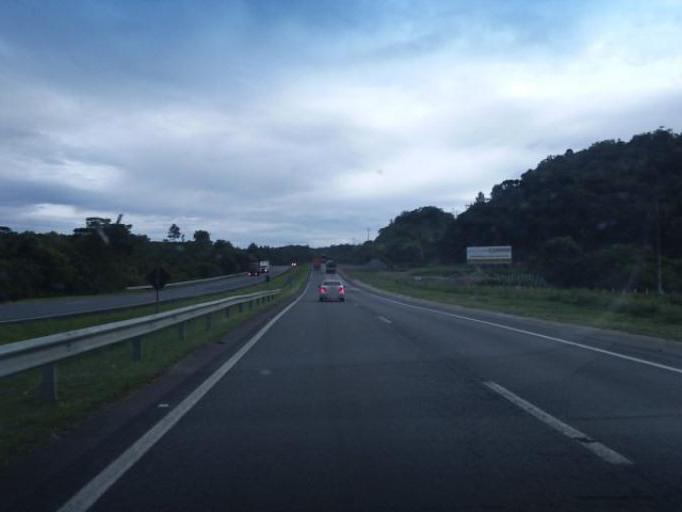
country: BR
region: Parana
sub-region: Campina Grande Do Sul
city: Campina Grande do Sul
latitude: -25.2584
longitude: -48.9136
